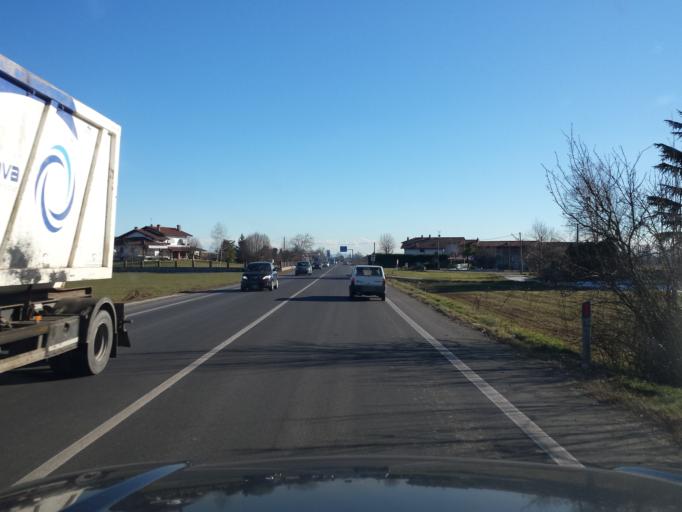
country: IT
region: Piedmont
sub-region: Provincia di Torino
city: Ozegna
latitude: 45.3589
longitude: 7.7313
